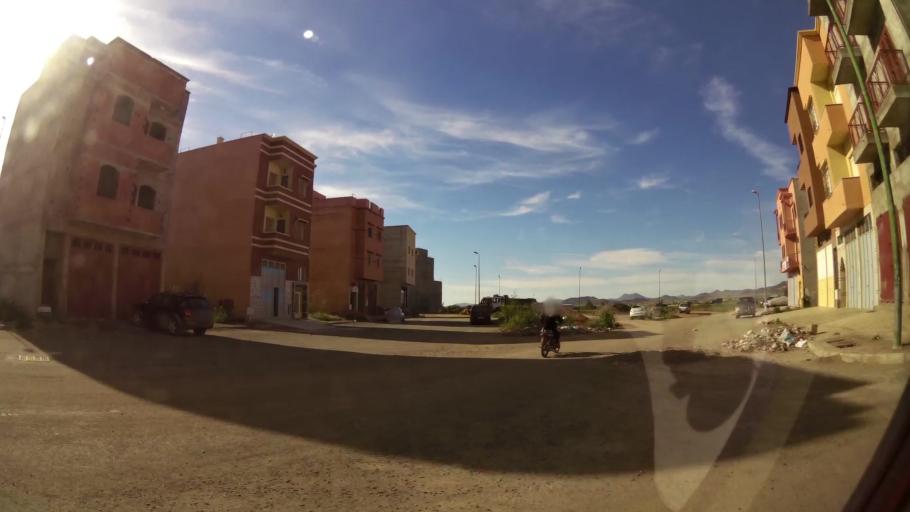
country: MA
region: Marrakech-Tensift-Al Haouz
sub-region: Marrakech
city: Marrakesh
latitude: 31.6810
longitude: -8.0445
